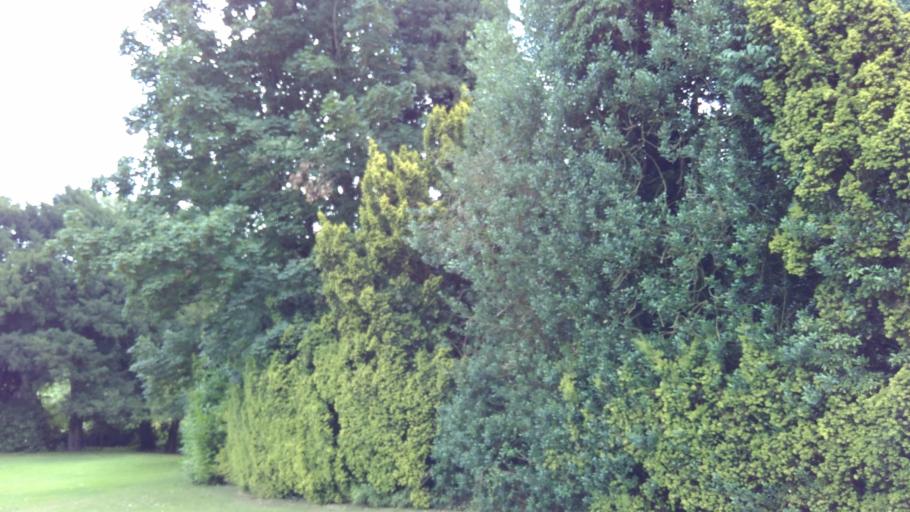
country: GB
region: England
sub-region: Hampshire
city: Highclere
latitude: 51.3256
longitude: -1.3591
